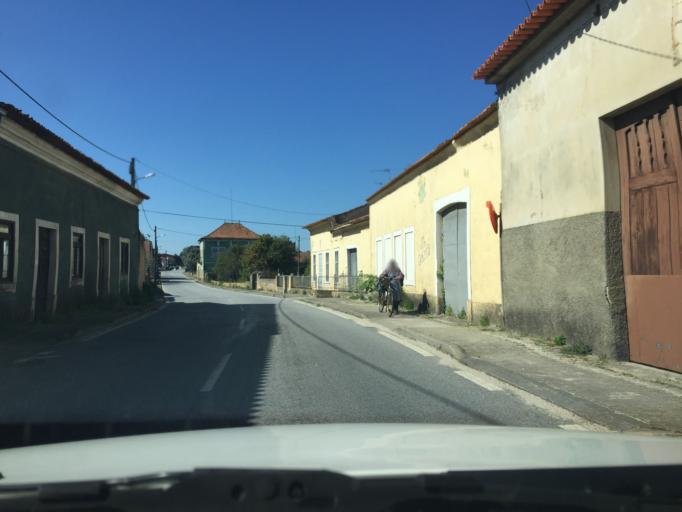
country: PT
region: Aveiro
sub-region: Anadia
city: Sangalhos
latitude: 40.4332
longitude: -8.5103
